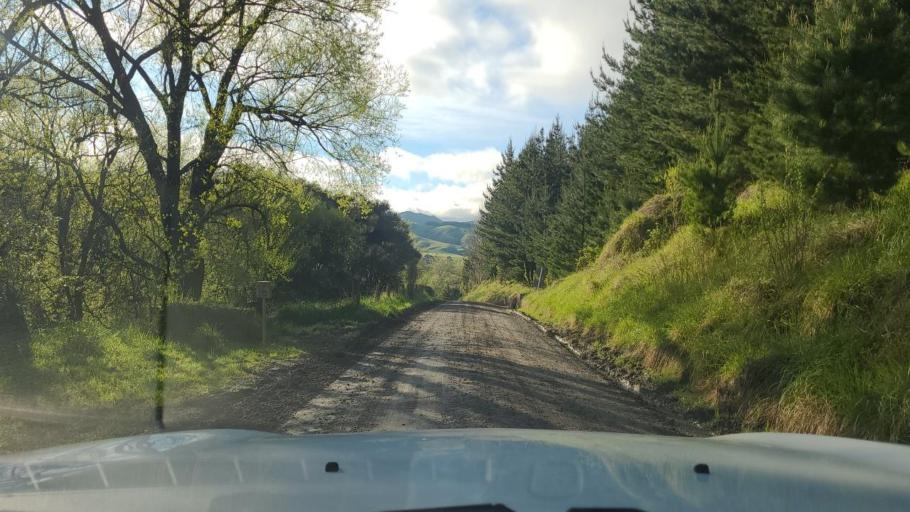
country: NZ
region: Wellington
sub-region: Masterton District
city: Masterton
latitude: -41.1883
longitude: 175.6721
